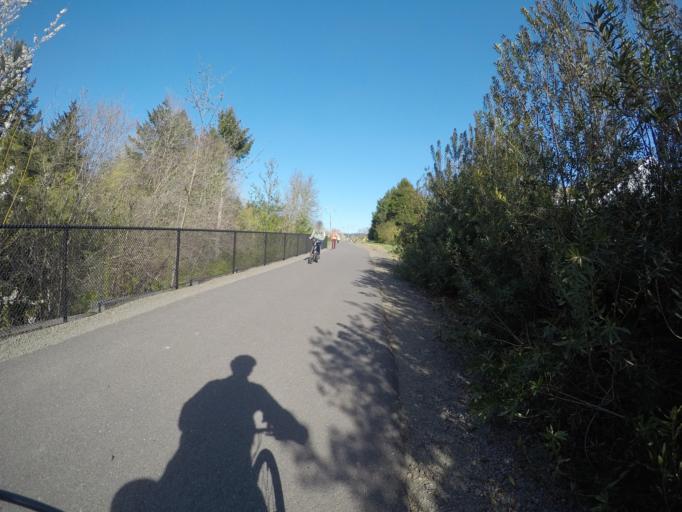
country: US
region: Oregon
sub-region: Washington County
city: Oak Hills
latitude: 45.5612
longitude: -122.8315
